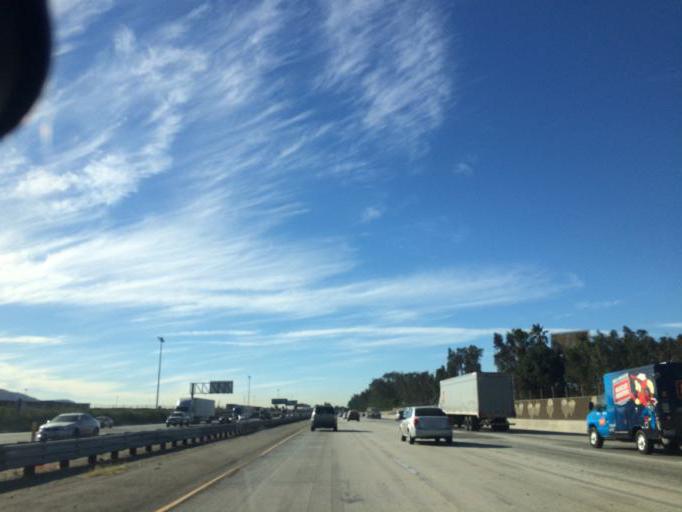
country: US
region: California
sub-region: San Bernardino County
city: Bloomington
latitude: 34.0686
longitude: -117.3774
